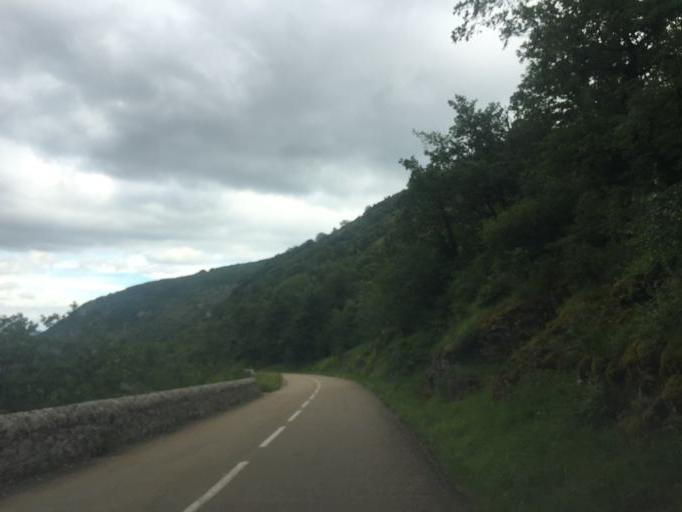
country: FR
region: Rhone-Alpes
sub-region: Departement de l'Ardeche
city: Saint-Priest
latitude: 44.6994
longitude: 4.5651
